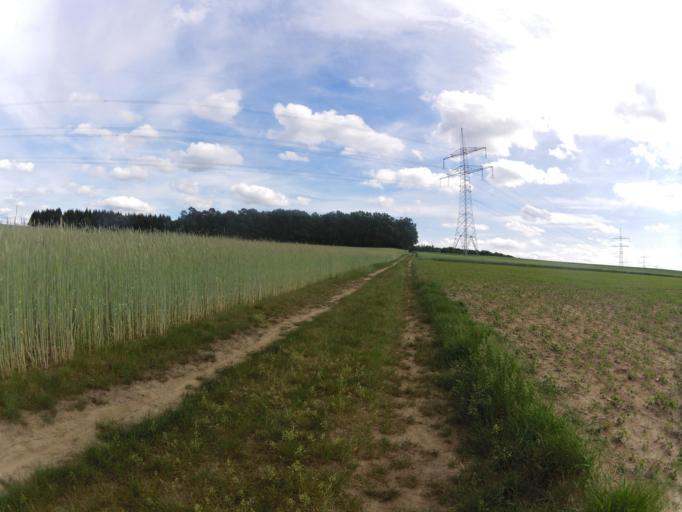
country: DE
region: Bavaria
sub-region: Regierungsbezirk Unterfranken
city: Ochsenfurt
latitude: 49.6989
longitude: 10.0682
